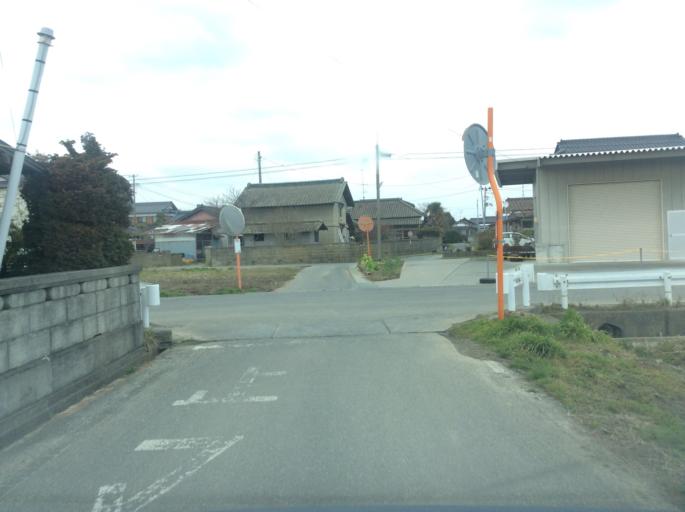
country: JP
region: Fukushima
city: Iwaki
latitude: 37.0807
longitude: 140.9737
